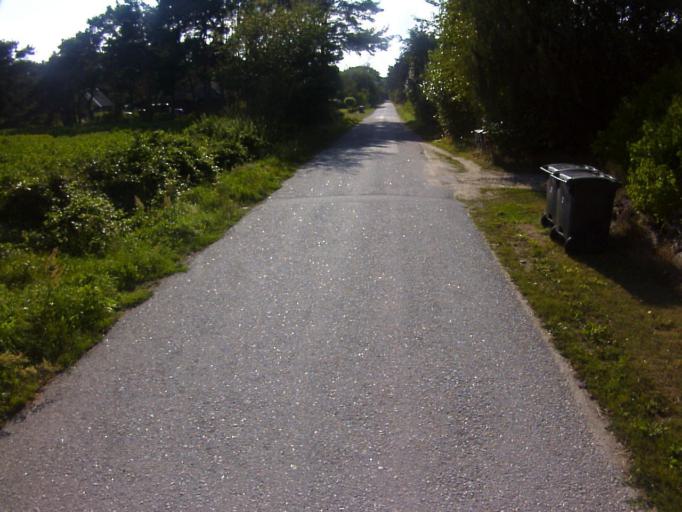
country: SE
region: Blekinge
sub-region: Solvesborgs Kommun
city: Soelvesborg
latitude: 56.0324
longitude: 14.7074
